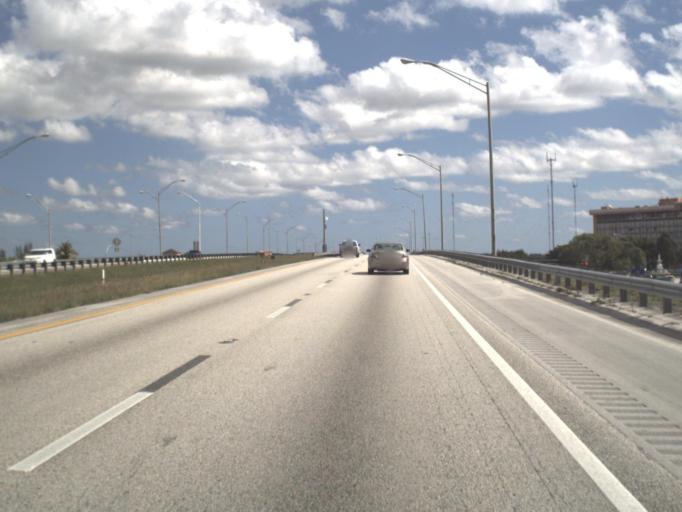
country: US
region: Florida
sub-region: Miami-Dade County
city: Lake Lucerne
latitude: 25.9722
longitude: -80.2495
